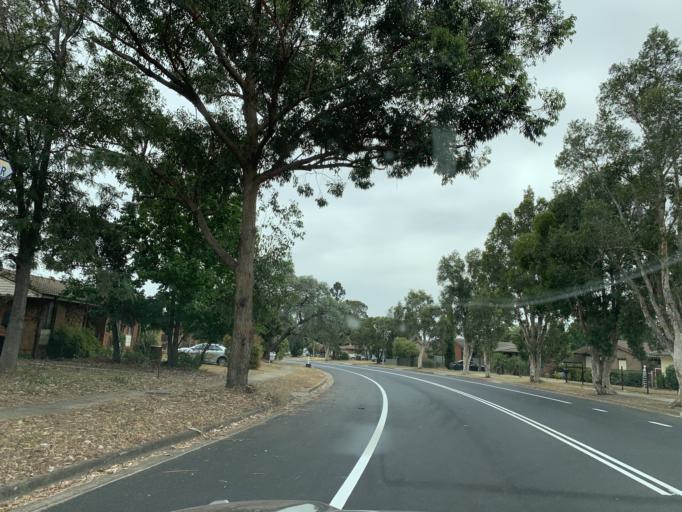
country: AU
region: New South Wales
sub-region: Blacktown
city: Doonside
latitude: -33.7520
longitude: 150.8755
